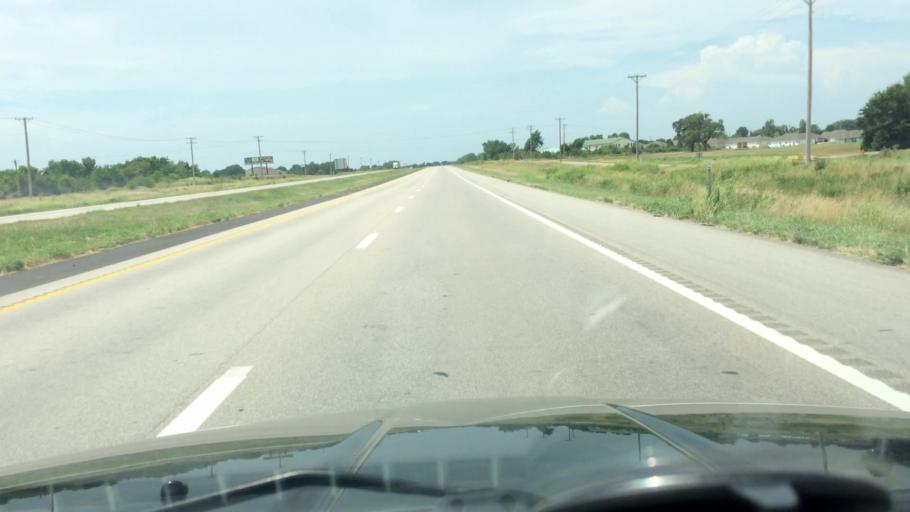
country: US
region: Missouri
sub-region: Polk County
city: Bolivar
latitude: 37.5842
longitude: -93.4149
